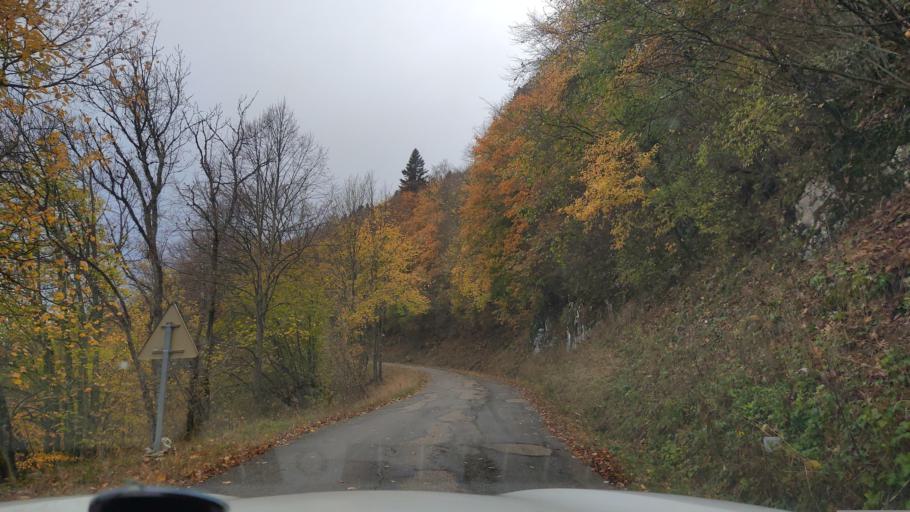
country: FR
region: Rhone-Alpes
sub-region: Departement de la Savoie
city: Le Bourget-du-Lac
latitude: 45.6440
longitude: 5.8106
